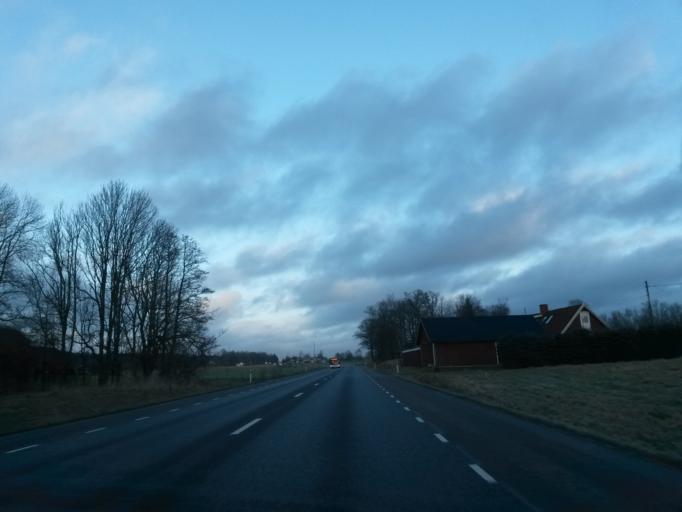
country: SE
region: Halland
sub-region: Halmstads Kommun
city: Aled
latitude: 56.7404
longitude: 12.9233
